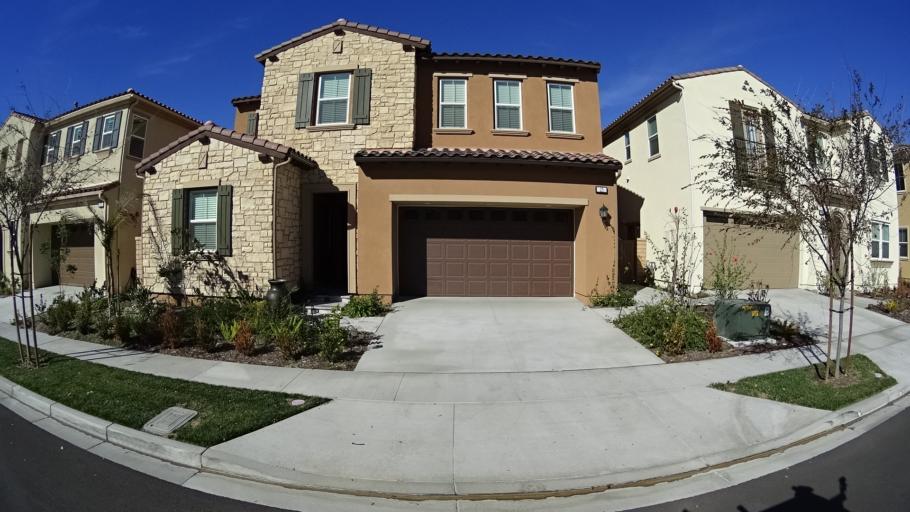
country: US
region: California
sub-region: Orange County
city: Foothill Ranch
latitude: 33.6735
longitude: -117.6777
